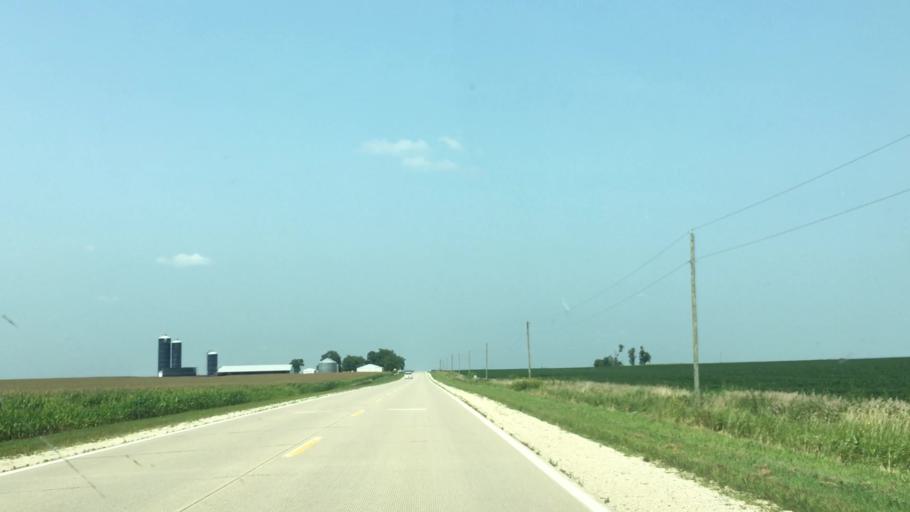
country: US
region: Iowa
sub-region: Fayette County
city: Fayette
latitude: 42.7387
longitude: -91.8040
